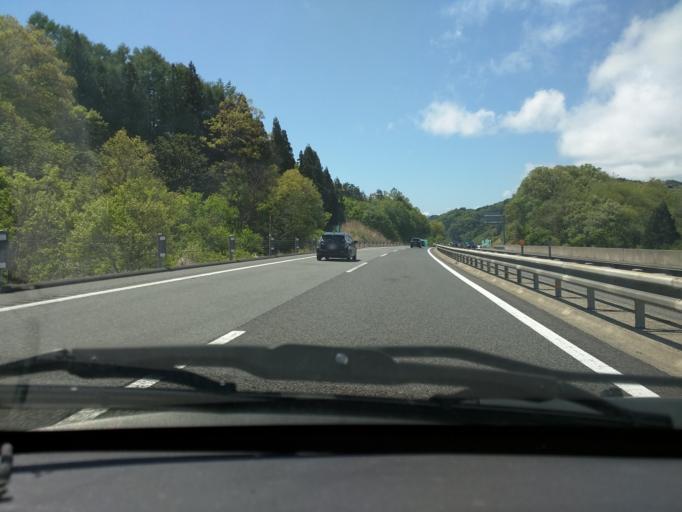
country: JP
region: Nagano
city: Nakano
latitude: 36.7912
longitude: 138.3219
